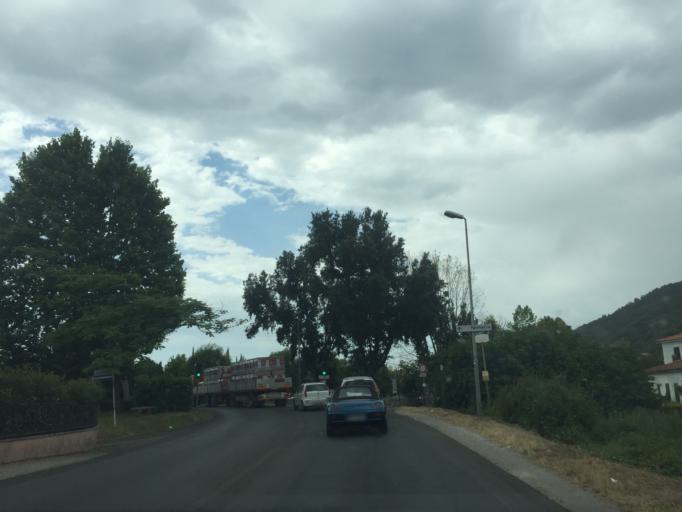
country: IT
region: Tuscany
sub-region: Province of Pisa
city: San Giuliano Terme
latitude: 43.7591
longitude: 10.4425
